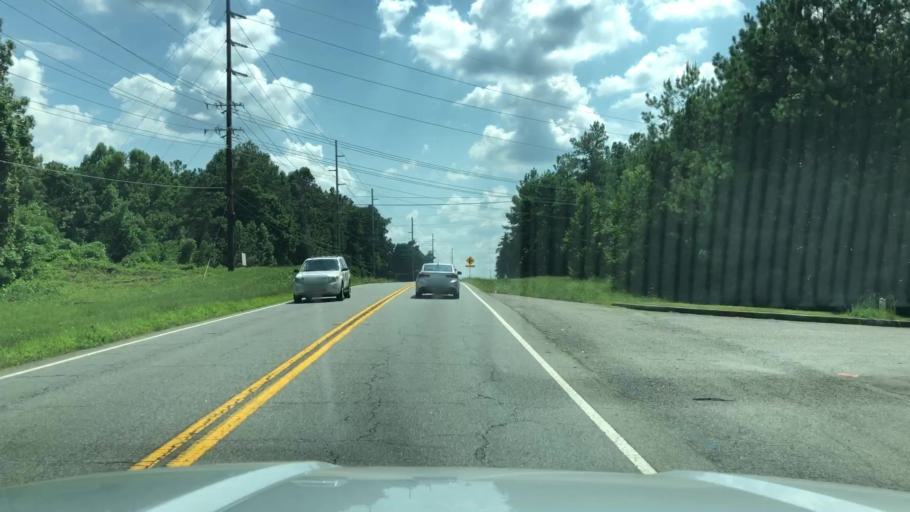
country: US
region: Georgia
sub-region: Cobb County
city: Acworth
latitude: 34.0047
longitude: -84.7001
